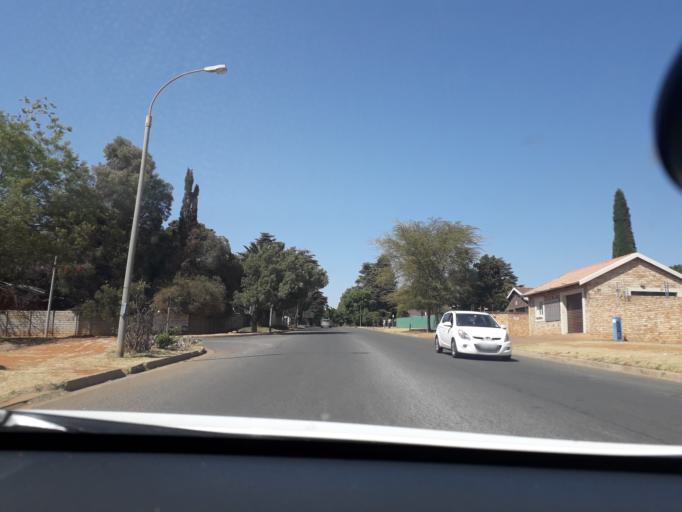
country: ZA
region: Gauteng
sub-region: City of Johannesburg Metropolitan Municipality
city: Modderfontein
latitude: -26.0613
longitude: 28.2119
